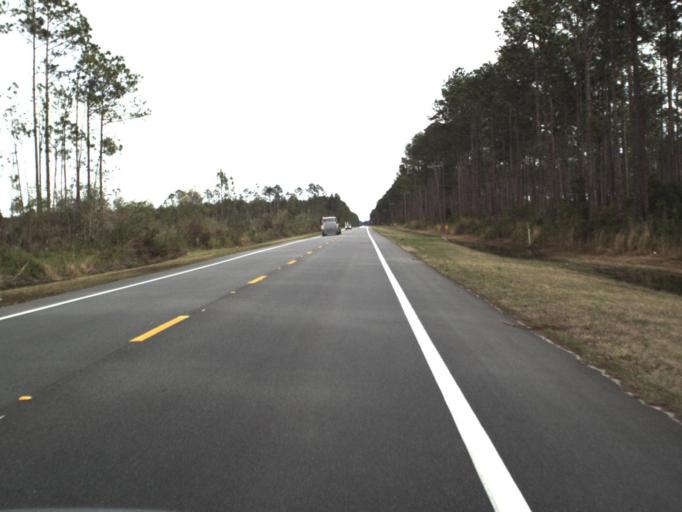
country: US
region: Florida
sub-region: Bay County
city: Callaway
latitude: 30.1394
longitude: -85.3965
